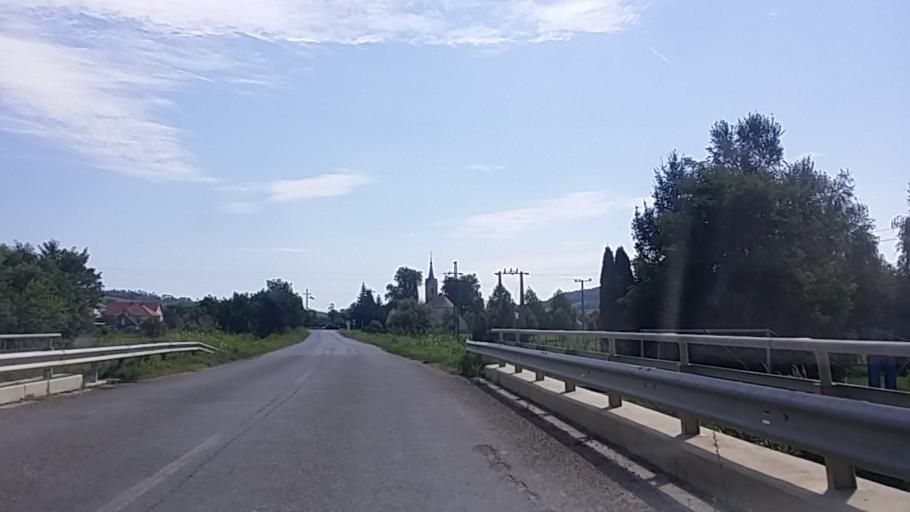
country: HU
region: Baranya
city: Sasd
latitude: 46.2223
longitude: 18.1175
